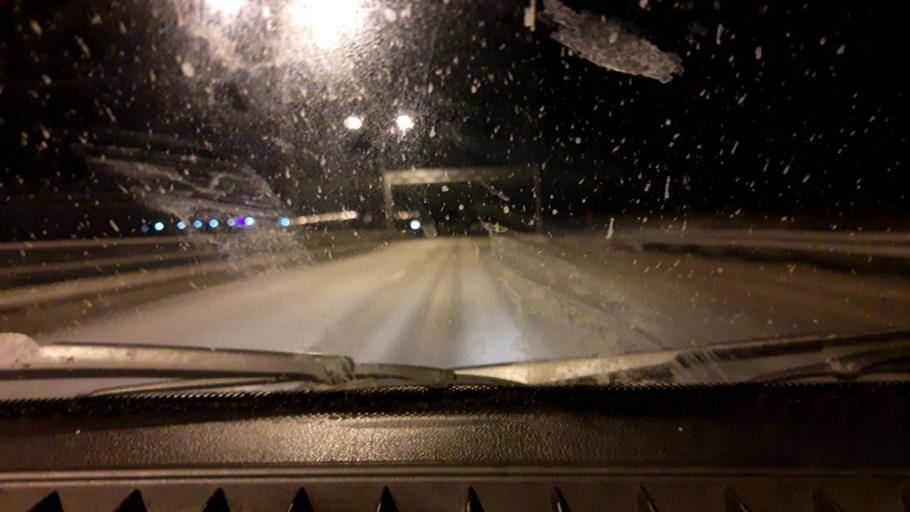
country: RU
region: Bashkortostan
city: Kushnarenkovo
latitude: 55.0702
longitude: 55.2941
